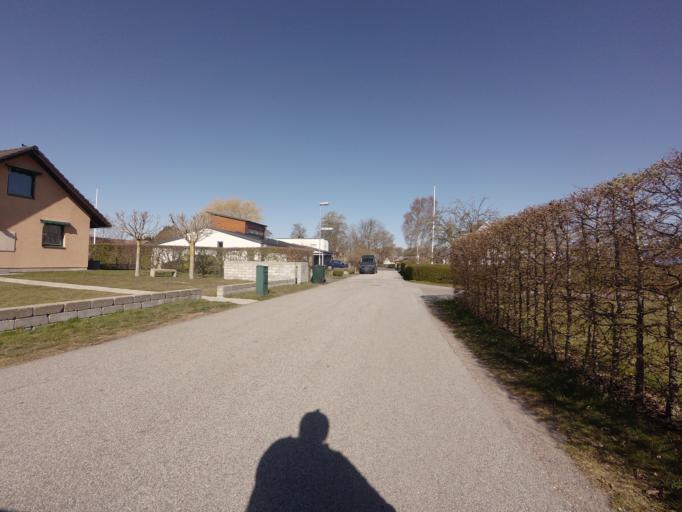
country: SE
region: Skane
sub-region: Lomma Kommun
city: Lomma
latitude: 55.6984
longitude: 13.0524
